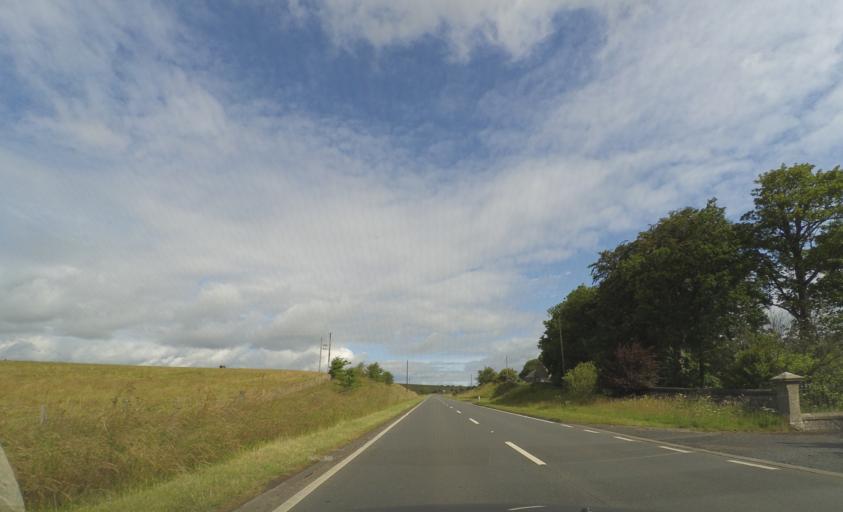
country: GB
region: Scotland
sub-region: The Scottish Borders
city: Hawick
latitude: 55.4499
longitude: -2.7775
